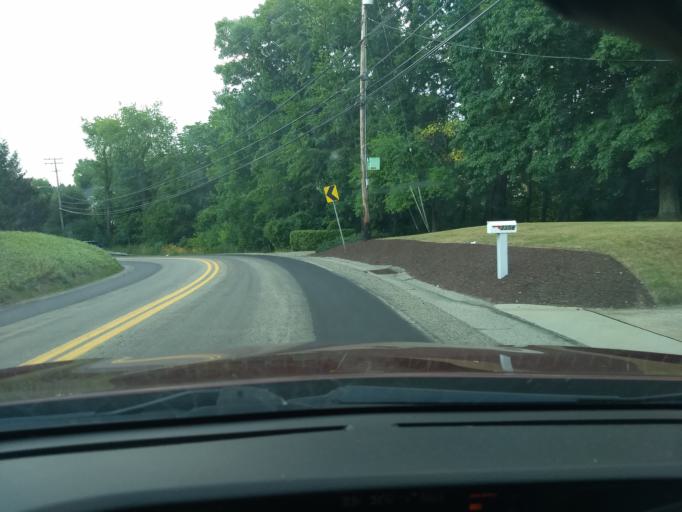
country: US
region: Pennsylvania
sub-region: Allegheny County
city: Plum
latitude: 40.4827
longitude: -79.7377
